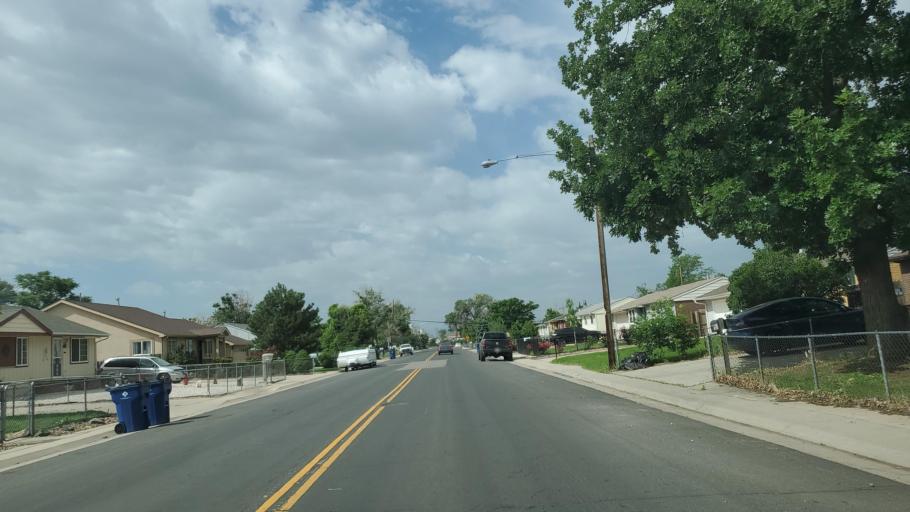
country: US
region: Colorado
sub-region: Adams County
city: Derby
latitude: 39.8387
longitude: -104.9162
